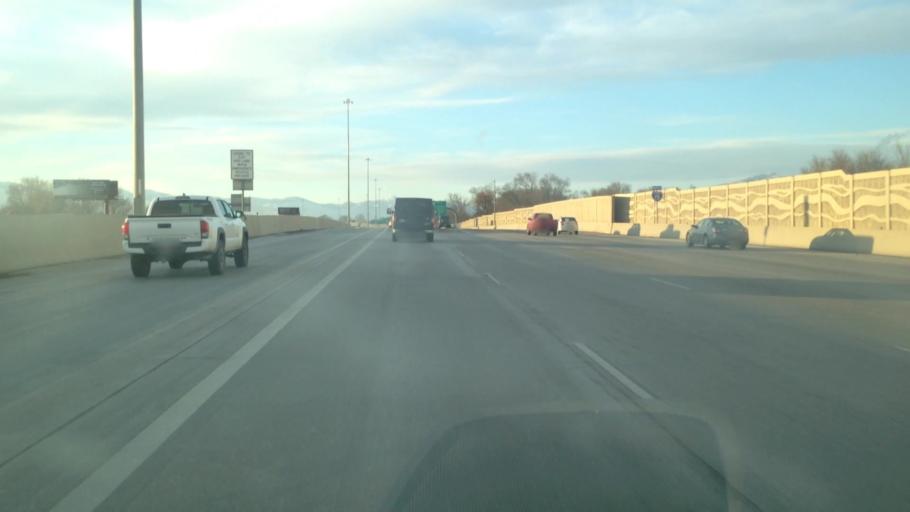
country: US
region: Utah
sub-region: Utah County
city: American Fork
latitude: 40.3659
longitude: -111.7949
